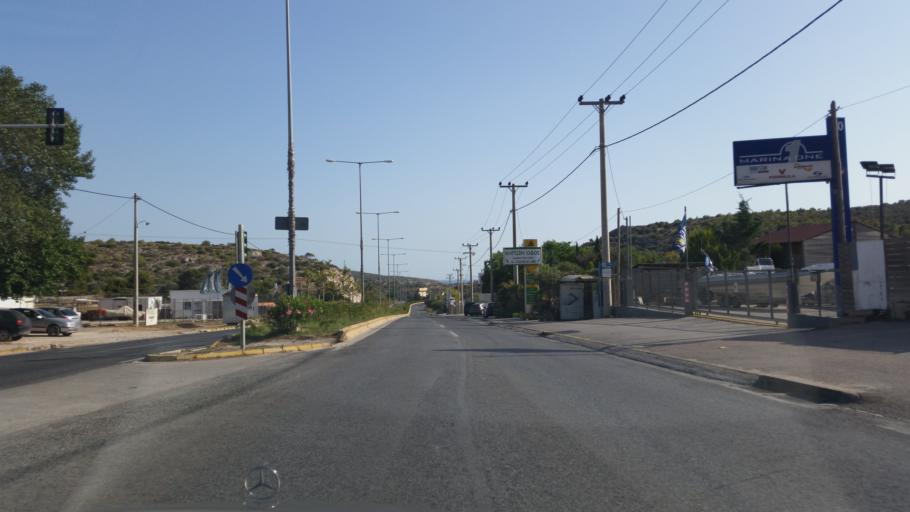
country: GR
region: Attica
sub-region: Nomarchia Anatolikis Attikis
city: Kitsi
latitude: 37.8537
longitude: 23.8307
